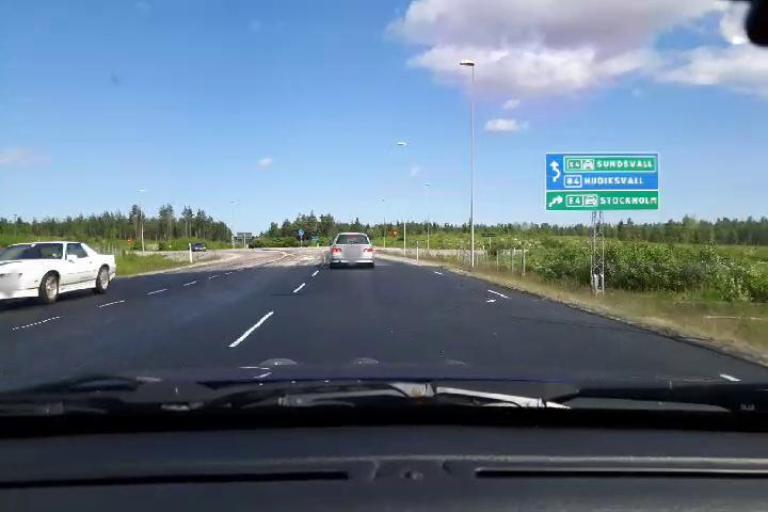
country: SE
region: Gaevleborg
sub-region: Hudiksvalls Kommun
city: Hudiksvall
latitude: 61.7139
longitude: 17.0451
